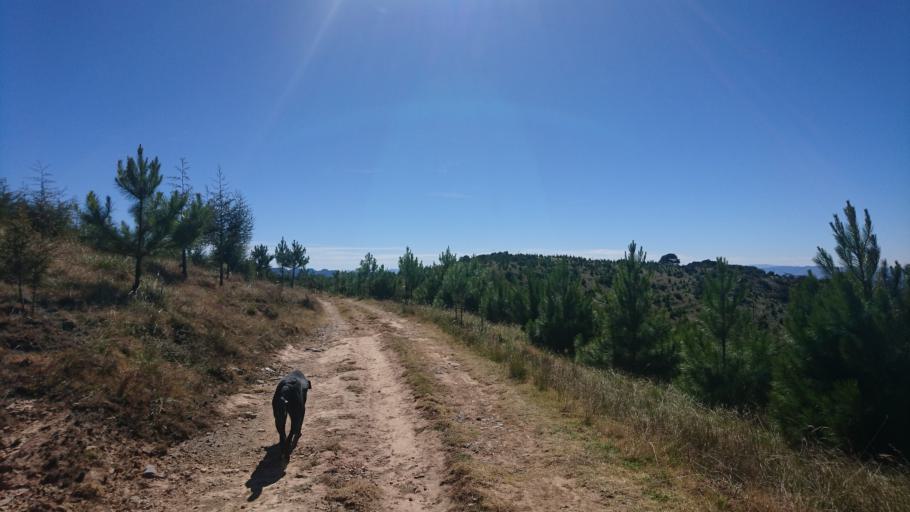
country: MX
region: San Luis Potosi
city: Zaragoza
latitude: 22.0171
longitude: -100.6214
